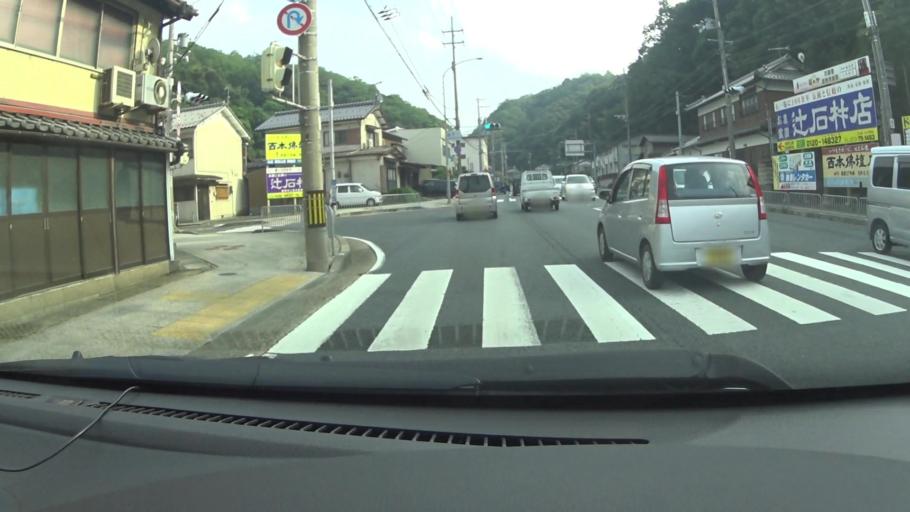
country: JP
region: Kyoto
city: Kameoka
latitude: 34.9894
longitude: 135.5973
